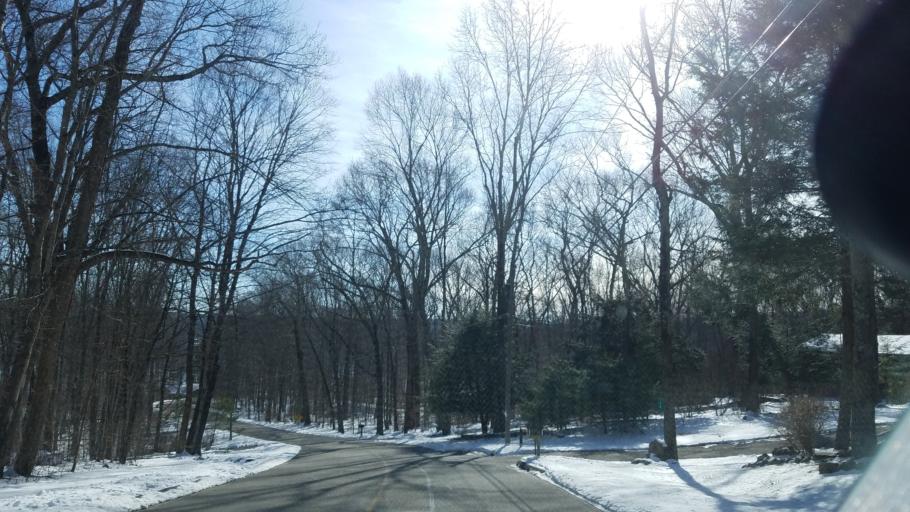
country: US
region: Connecticut
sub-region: Tolland County
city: Coventry Lake
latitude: 41.7253
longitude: -72.3632
